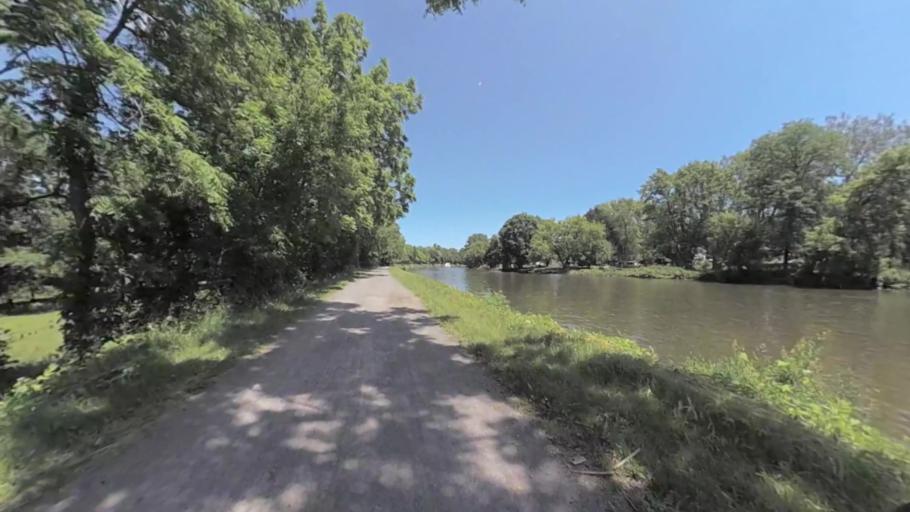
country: US
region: New York
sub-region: Monroe County
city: Fairport
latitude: 43.0826
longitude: -77.4598
